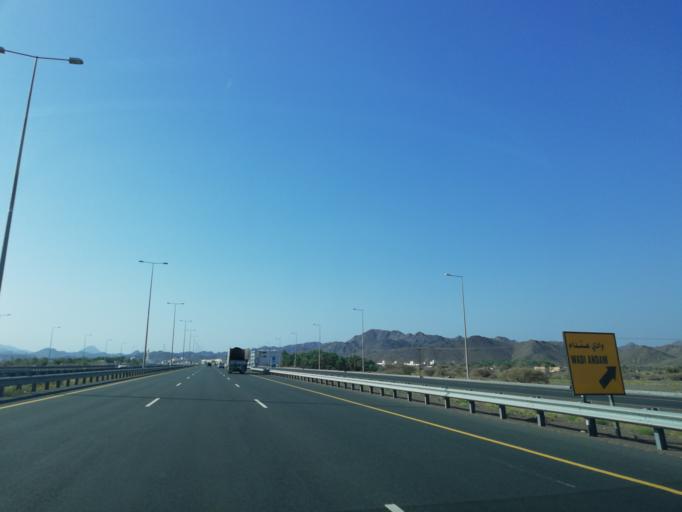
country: OM
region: Muhafazat ad Dakhiliyah
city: Sufalat Sama'il
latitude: 23.0320
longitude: 58.2048
